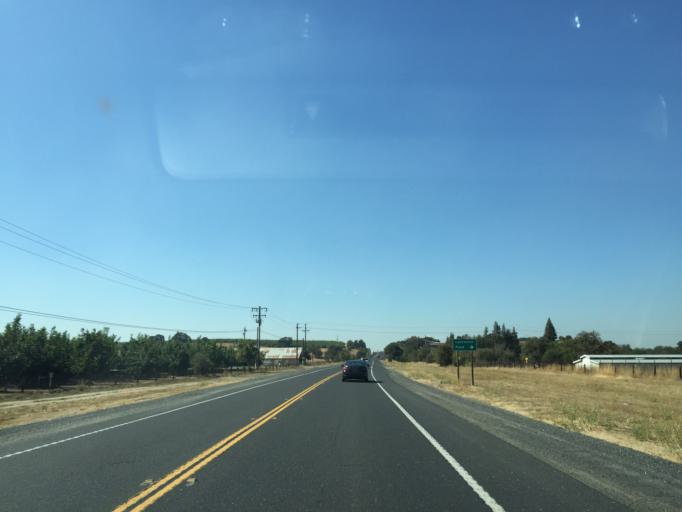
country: US
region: California
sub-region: Stanislaus County
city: East Oakdale
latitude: 37.7864
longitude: -120.7351
